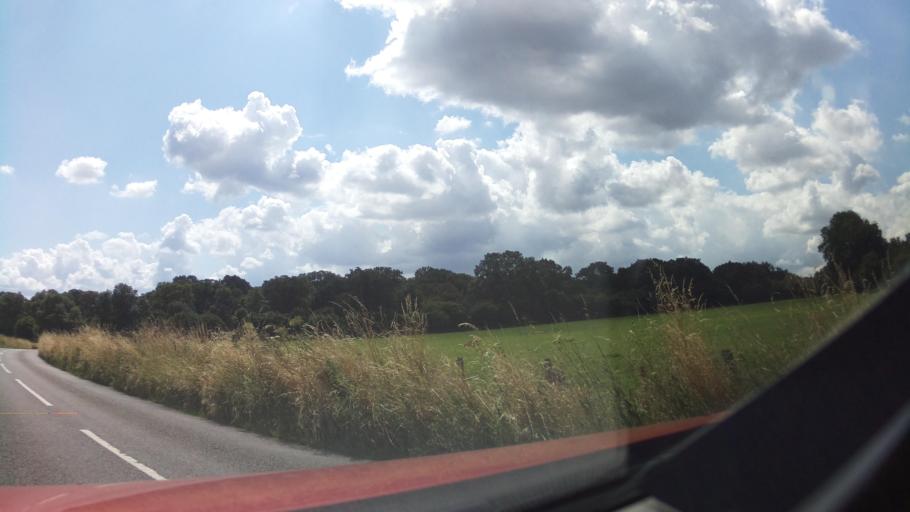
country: GB
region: England
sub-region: Borough of Swindon
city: Bishopstone
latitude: 51.5449
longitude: -1.5945
